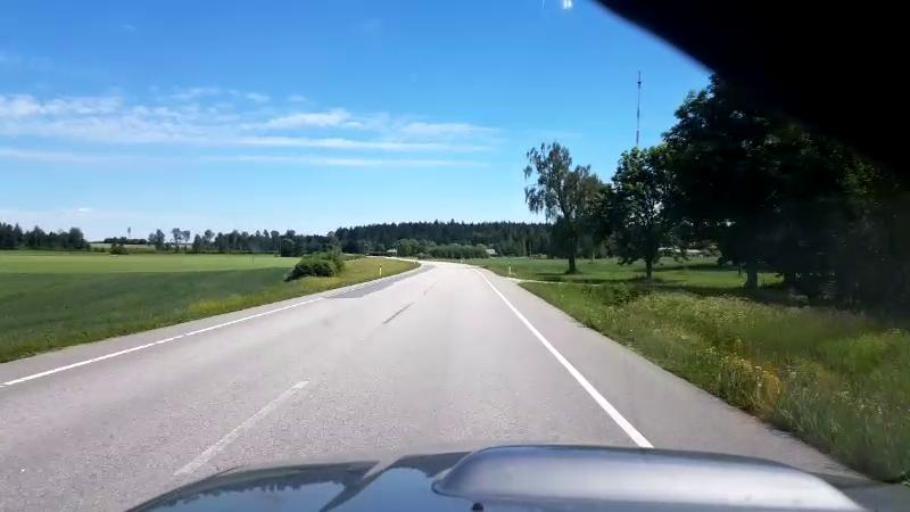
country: EE
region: Jaervamaa
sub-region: Koeru vald
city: Koeru
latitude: 58.9841
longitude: 26.0388
